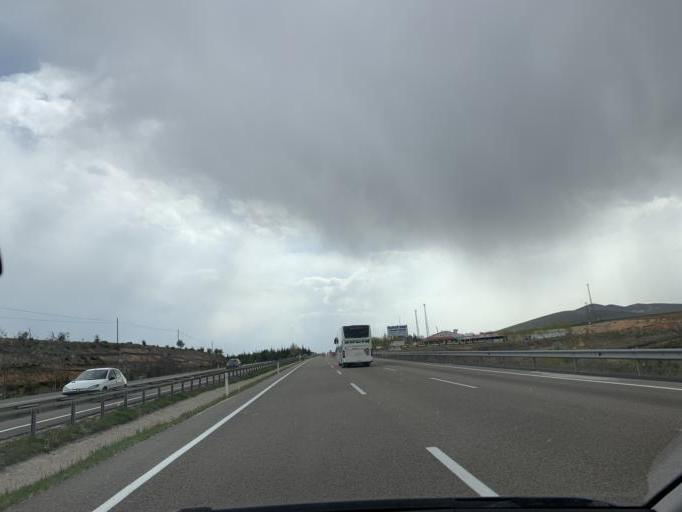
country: TR
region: Eskisehir
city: Sivrihisar
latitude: 39.5067
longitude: 31.6111
